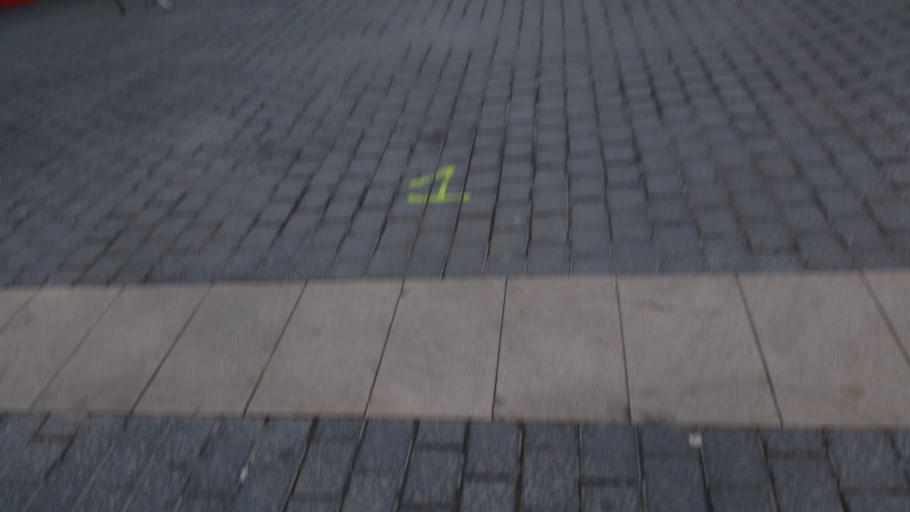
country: ES
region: Balearic Islands
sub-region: Illes Balears
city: Inca
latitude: 39.7197
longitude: 2.9075
